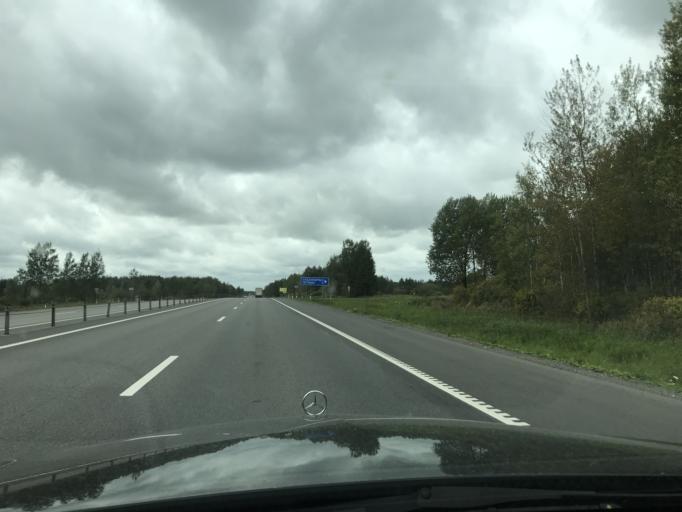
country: BY
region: Vitebsk
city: Dubrowna
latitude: 54.6790
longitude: 30.7540
